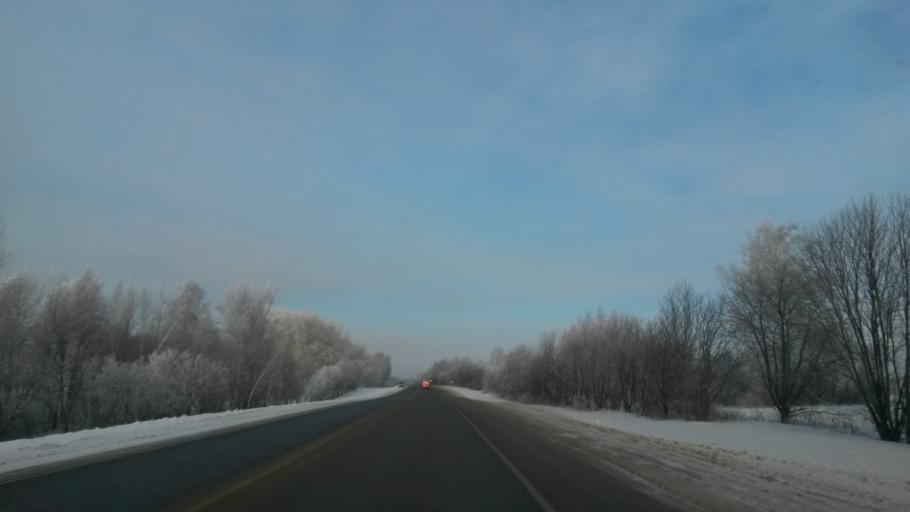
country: RU
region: Vladimir
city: Bogolyubovo
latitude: 56.2006
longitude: 40.4456
